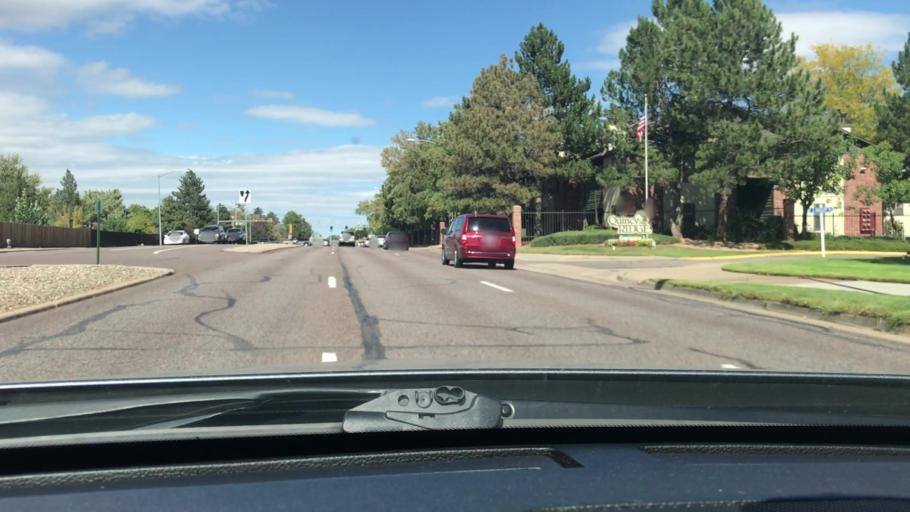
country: US
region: Colorado
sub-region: Arapahoe County
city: Dove Valley
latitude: 39.6368
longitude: -104.8102
